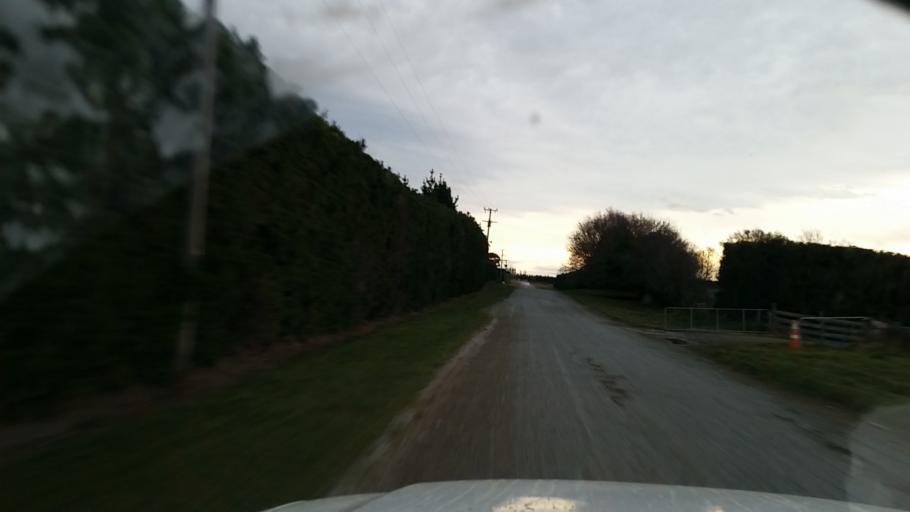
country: NZ
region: Canterbury
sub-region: Ashburton District
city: Ashburton
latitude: -43.8332
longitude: 171.6224
